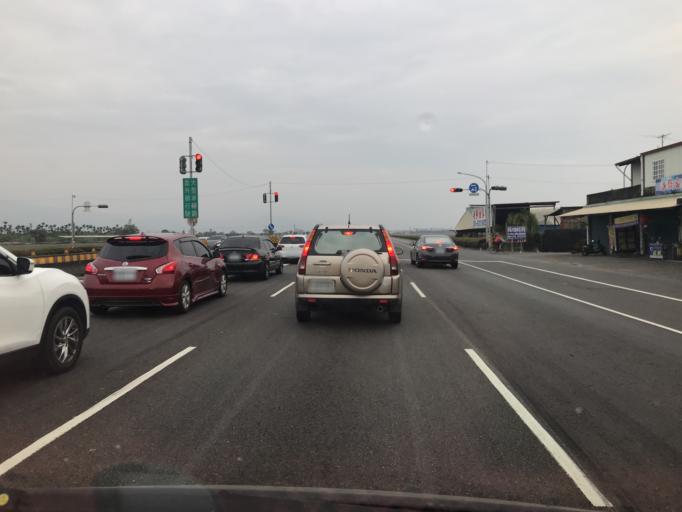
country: TW
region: Taiwan
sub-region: Pingtung
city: Pingtung
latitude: 22.4343
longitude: 120.5705
